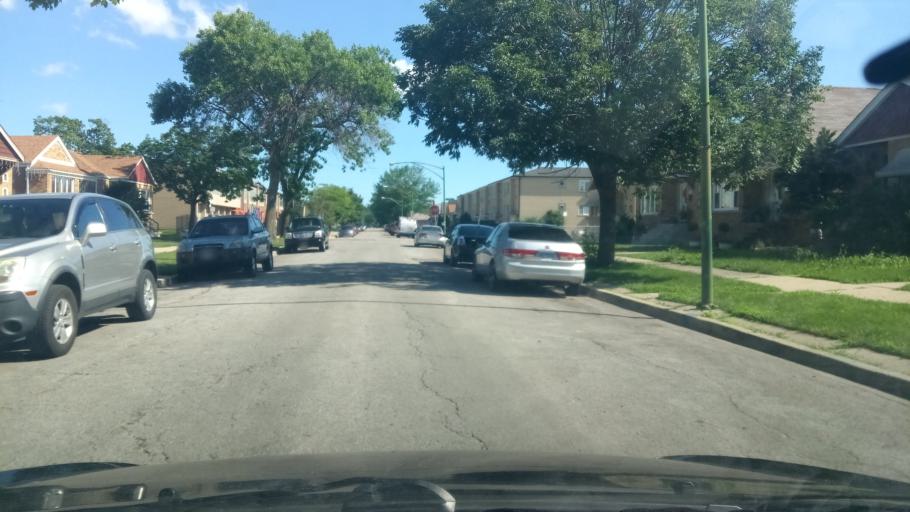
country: US
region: Illinois
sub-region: Cook County
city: Hometown
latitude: 41.7612
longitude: -87.7174
